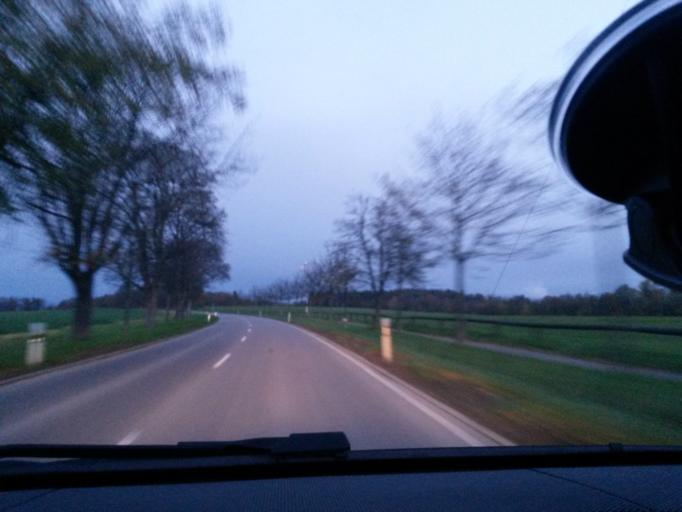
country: DE
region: Baden-Wuerttemberg
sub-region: Regierungsbezirk Stuttgart
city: Esslingen
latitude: 48.7598
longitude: 9.3367
